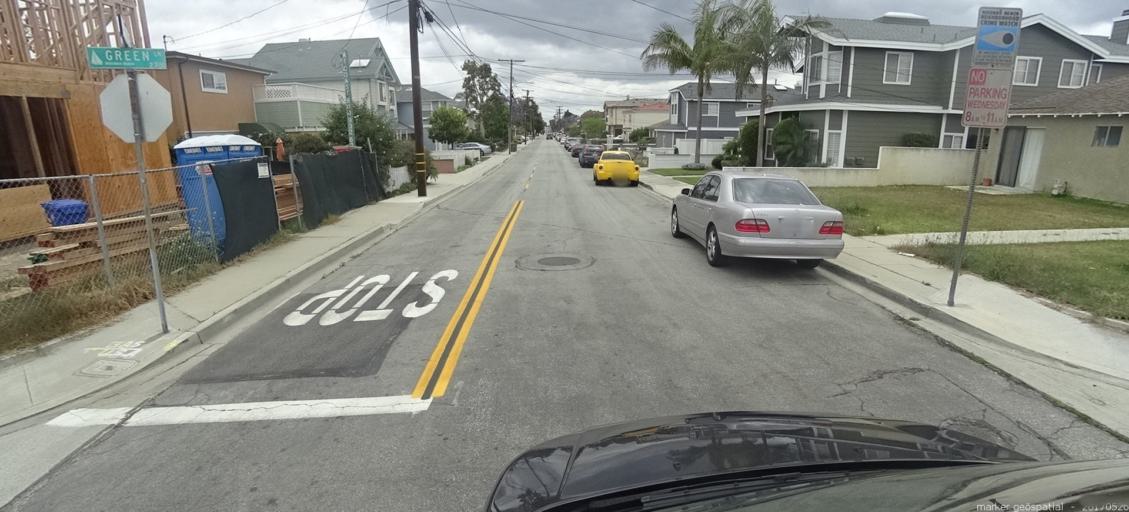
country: US
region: California
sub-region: Los Angeles County
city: Lawndale
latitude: 33.8794
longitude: -118.3770
